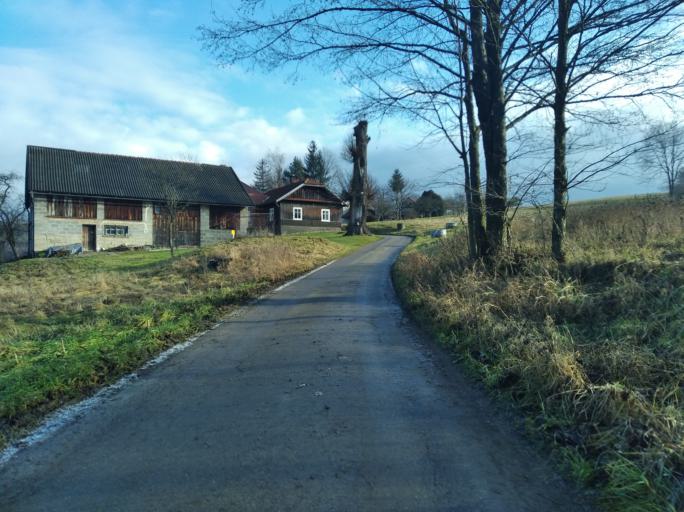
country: PL
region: Subcarpathian Voivodeship
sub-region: Powiat strzyzowski
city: Wysoka Strzyzowska
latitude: 49.8568
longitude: 21.7500
